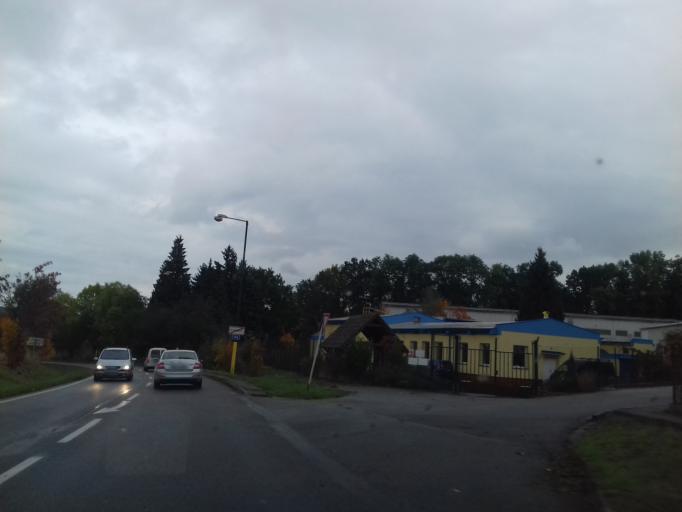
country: CZ
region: Pardubicky
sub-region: Okres Chrudim
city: Chrast
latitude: 49.8984
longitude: 15.9460
